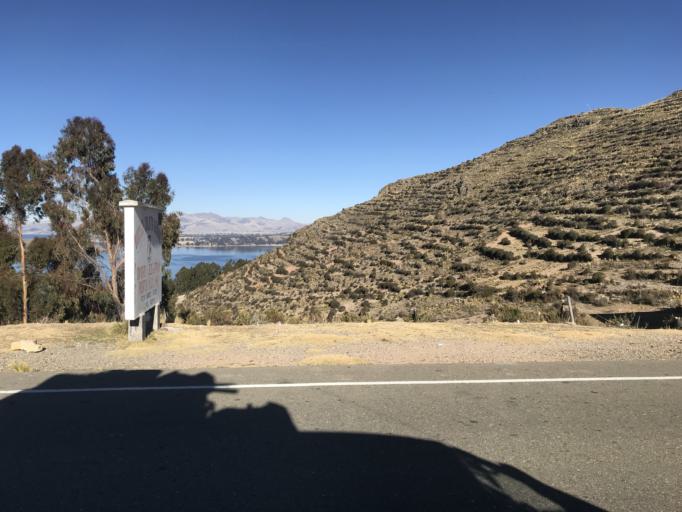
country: BO
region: La Paz
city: San Pedro
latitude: -16.1944
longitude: -68.9143
